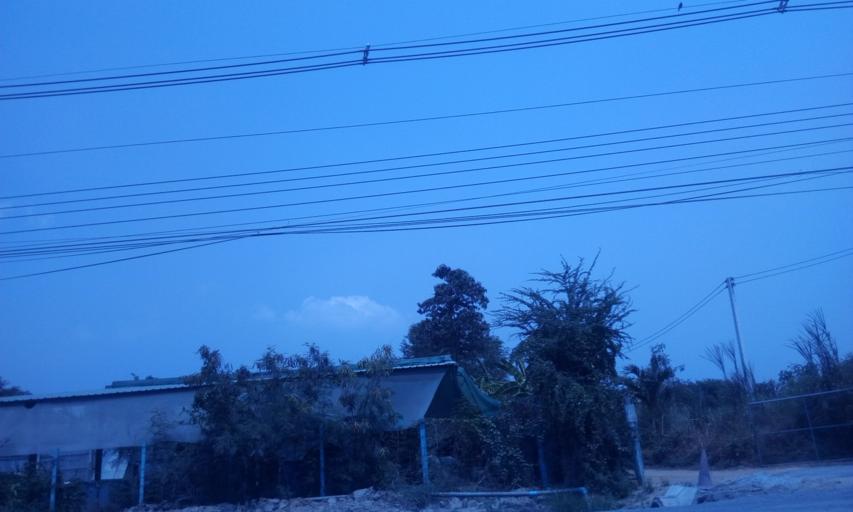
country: TH
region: Chachoengsao
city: Ban Pho
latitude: 13.5621
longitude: 101.1338
